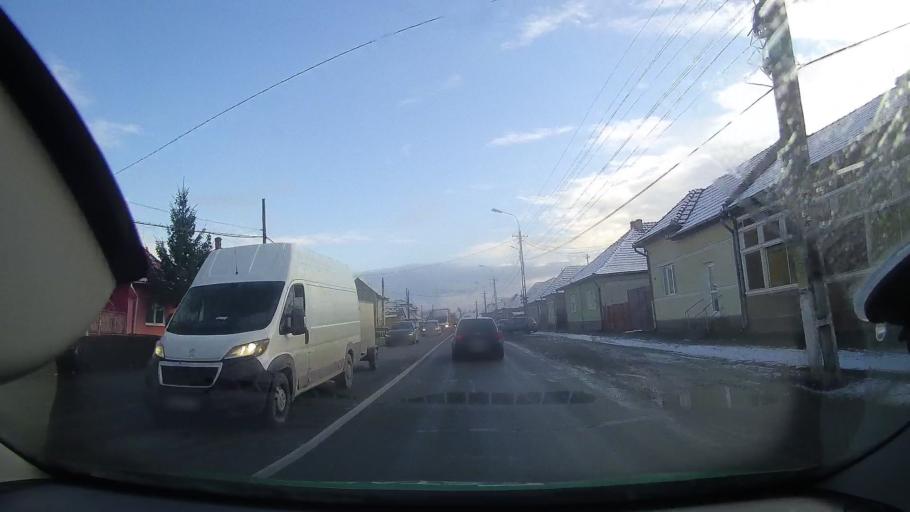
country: RO
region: Mures
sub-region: Comuna Iernut
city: Iernut
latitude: 46.4490
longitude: 24.2372
